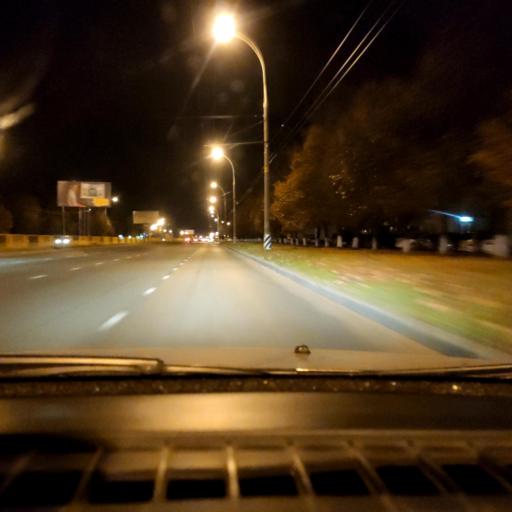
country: RU
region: Samara
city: Tol'yatti
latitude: 53.5244
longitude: 49.2960
